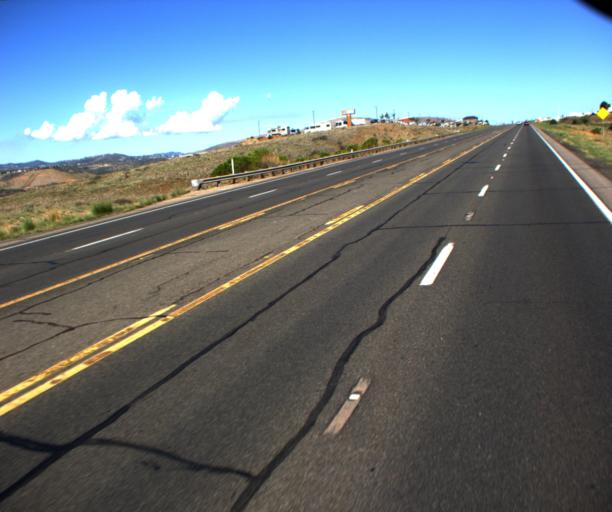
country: US
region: Arizona
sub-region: Yavapai County
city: Prescott Valley
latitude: 34.5823
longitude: -112.3060
